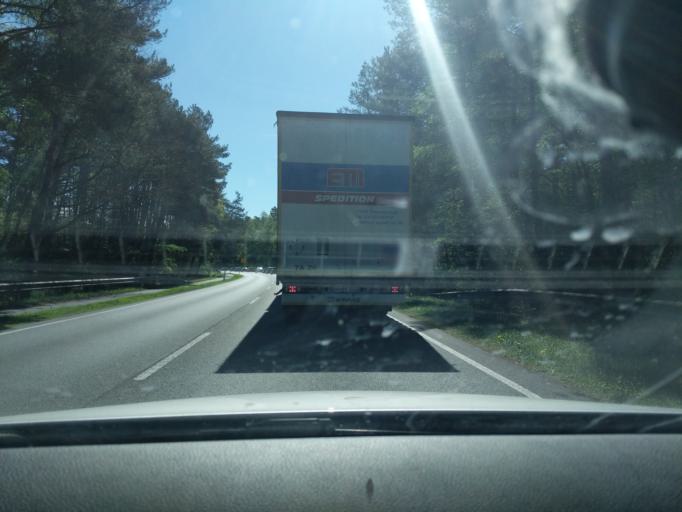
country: DE
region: Lower Saxony
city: Buxtehude
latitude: 53.4556
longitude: 9.7267
